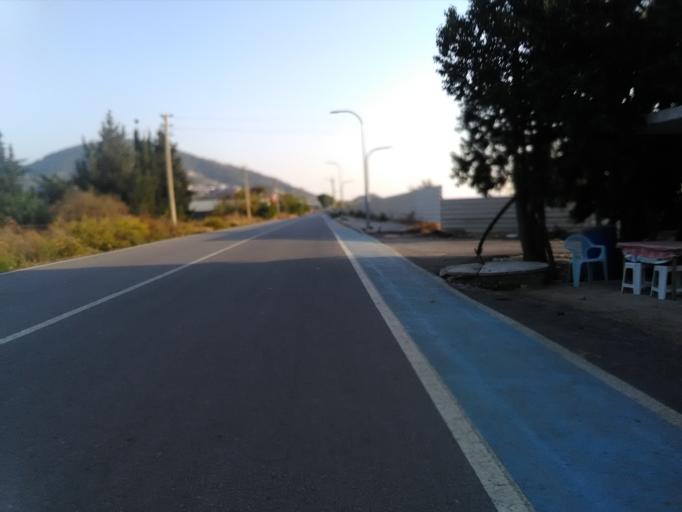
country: TR
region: Antalya
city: Gazipasa
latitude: 36.2535
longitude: 32.2914
